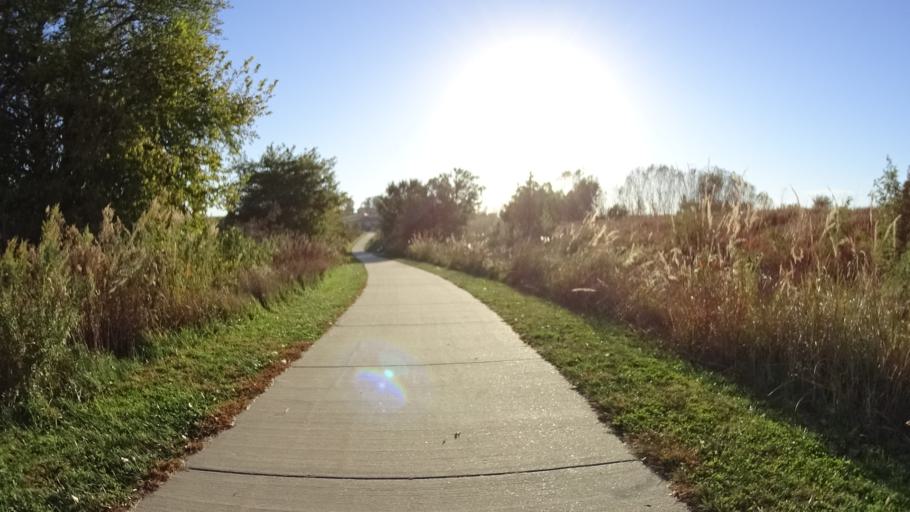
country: US
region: Nebraska
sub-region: Sarpy County
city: Papillion
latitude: 41.1365
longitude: -96.0722
